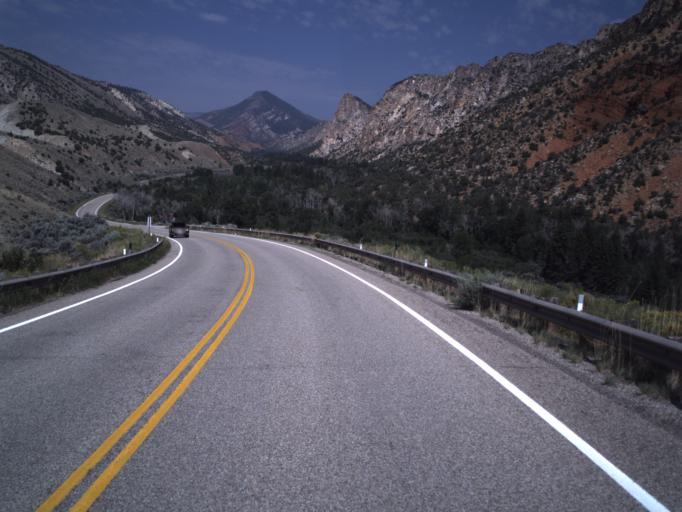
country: US
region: Utah
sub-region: Daggett County
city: Manila
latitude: 40.9196
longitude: -109.6947
